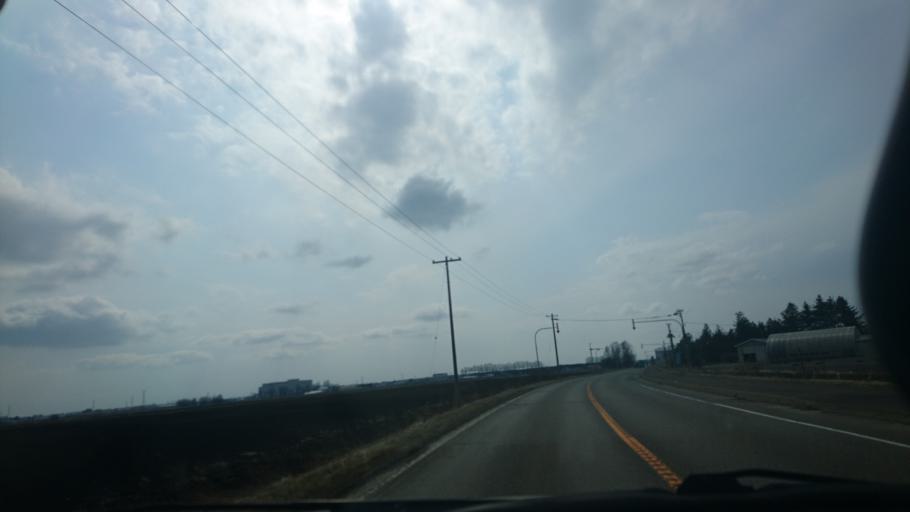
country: JP
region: Hokkaido
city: Otofuke
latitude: 43.1652
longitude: 143.2635
